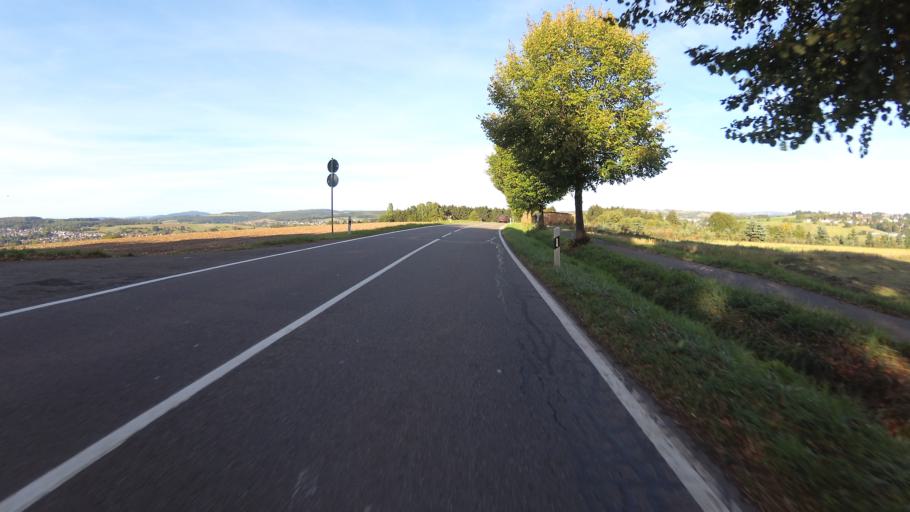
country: DE
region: Saarland
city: Illingen
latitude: 49.3626
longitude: 7.0311
